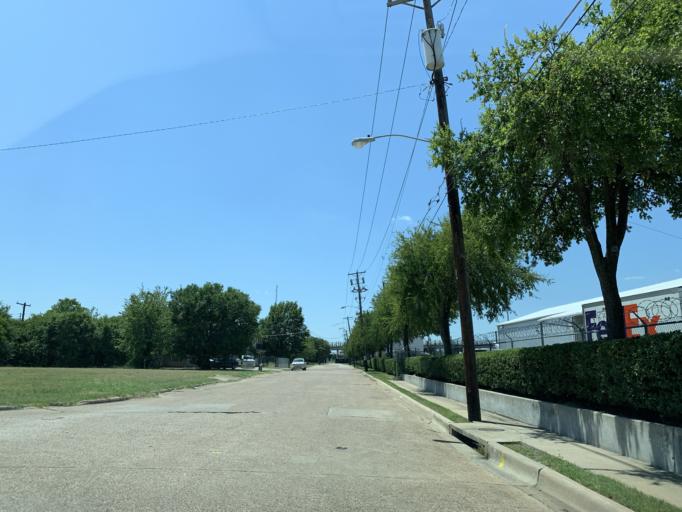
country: US
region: Texas
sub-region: Dallas County
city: Dallas
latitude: 32.7769
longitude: -96.7731
